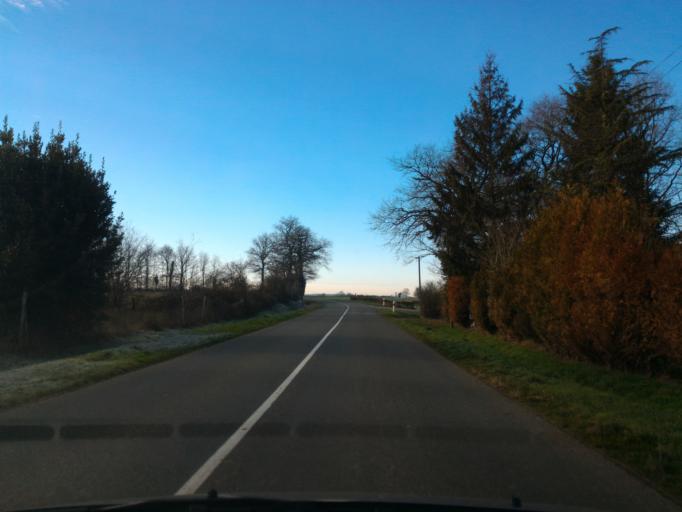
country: FR
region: Poitou-Charentes
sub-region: Departement de la Charente
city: Loubert
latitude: 46.0317
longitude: 0.5377
